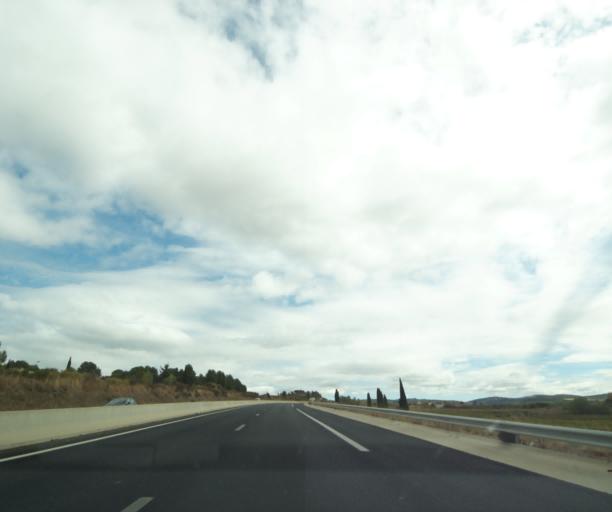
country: FR
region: Languedoc-Roussillon
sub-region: Departement de l'Herault
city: Gignac
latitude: 43.6445
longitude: 3.5601
